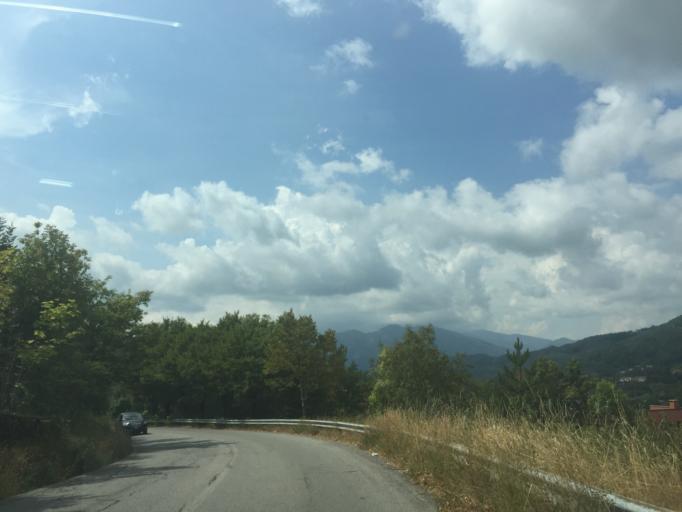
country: IT
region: Tuscany
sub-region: Provincia di Pistoia
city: Campo Tizzoro
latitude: 44.0431
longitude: 10.8338
